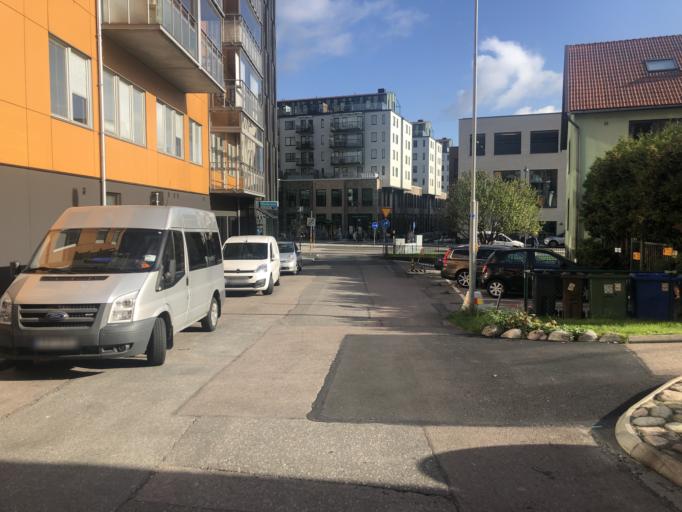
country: SE
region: Vaestra Goetaland
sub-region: Molndal
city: Moelndal
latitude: 57.6548
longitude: 12.0110
